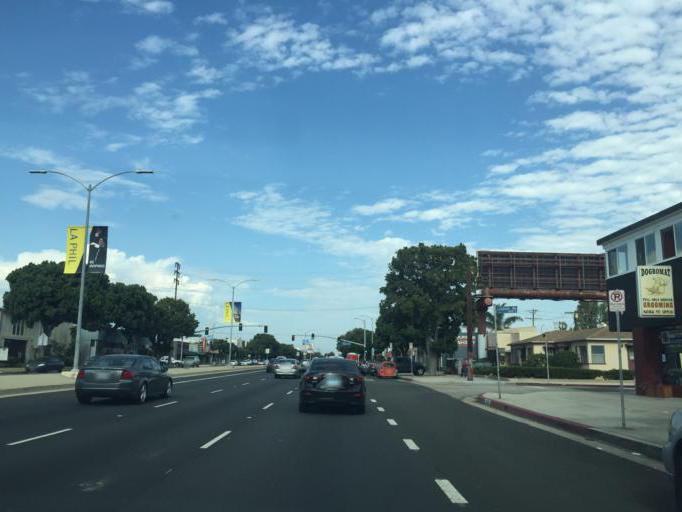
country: US
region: California
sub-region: Los Angeles County
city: Marina del Rey
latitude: 33.9992
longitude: -118.4424
